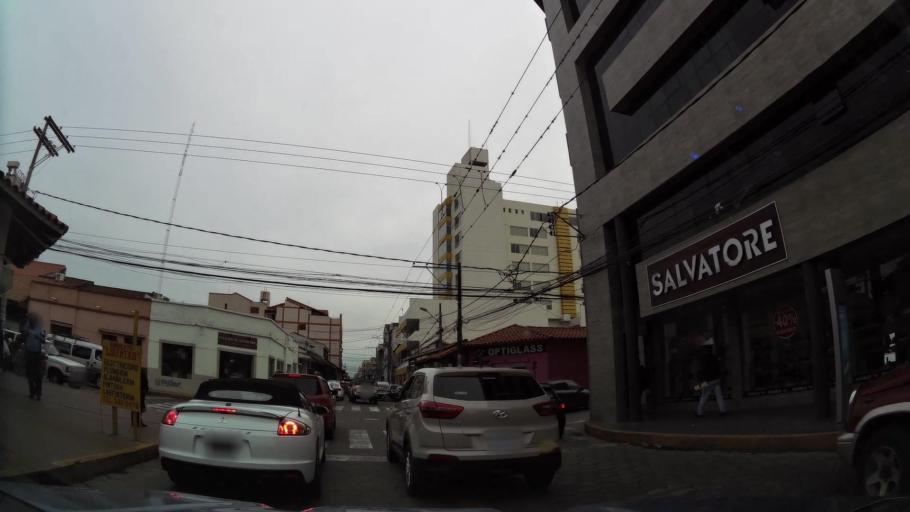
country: BO
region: Santa Cruz
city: Santa Cruz de la Sierra
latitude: -17.7786
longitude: -63.1831
